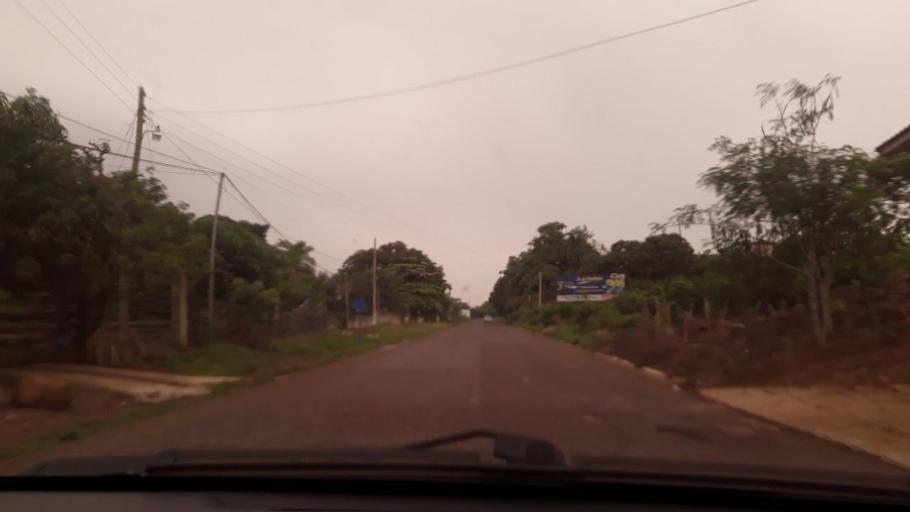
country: GT
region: Jutiapa
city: Asuncion Mita
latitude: 14.3923
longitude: -89.7242
